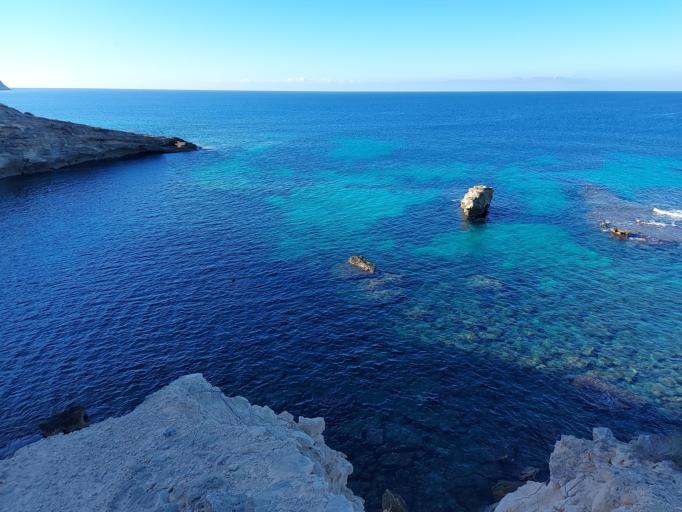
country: ES
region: Balearic Islands
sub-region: Illes Balears
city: s'Arenal
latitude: 39.4491
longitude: 2.7439
